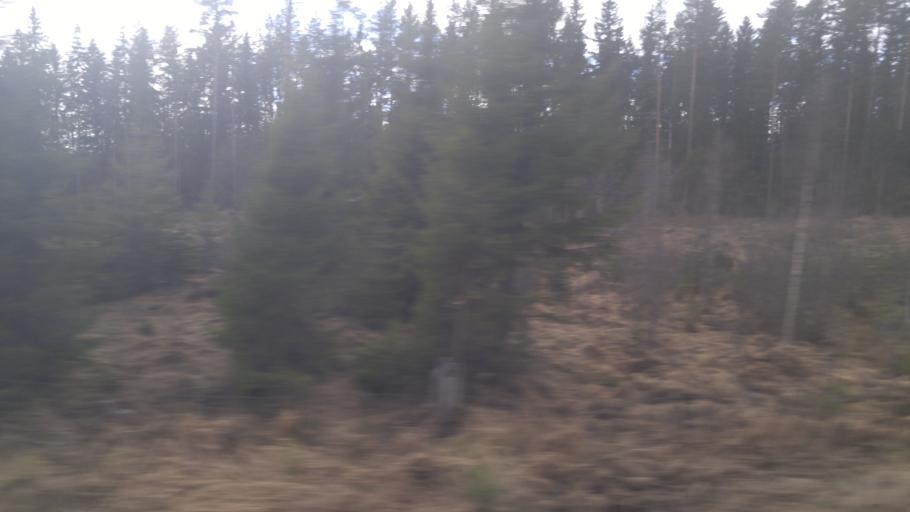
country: NO
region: Hedmark
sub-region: Stange
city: Stange
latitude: 60.6660
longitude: 11.2245
